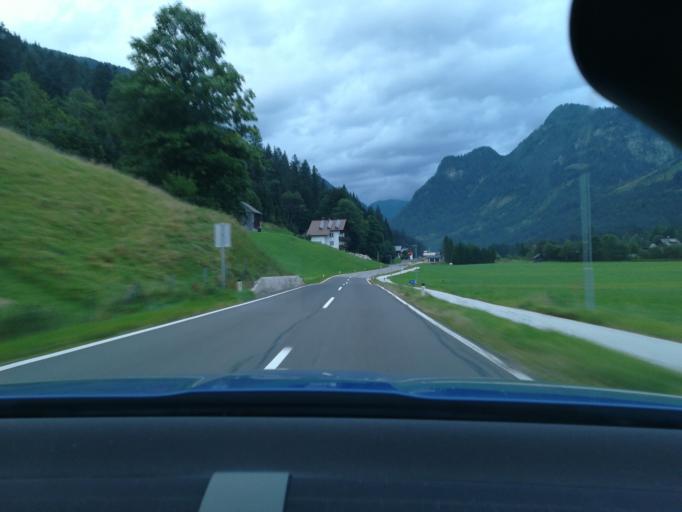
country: AT
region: Upper Austria
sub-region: Politischer Bezirk Gmunden
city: Bad Goisern
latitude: 47.5880
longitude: 13.5492
